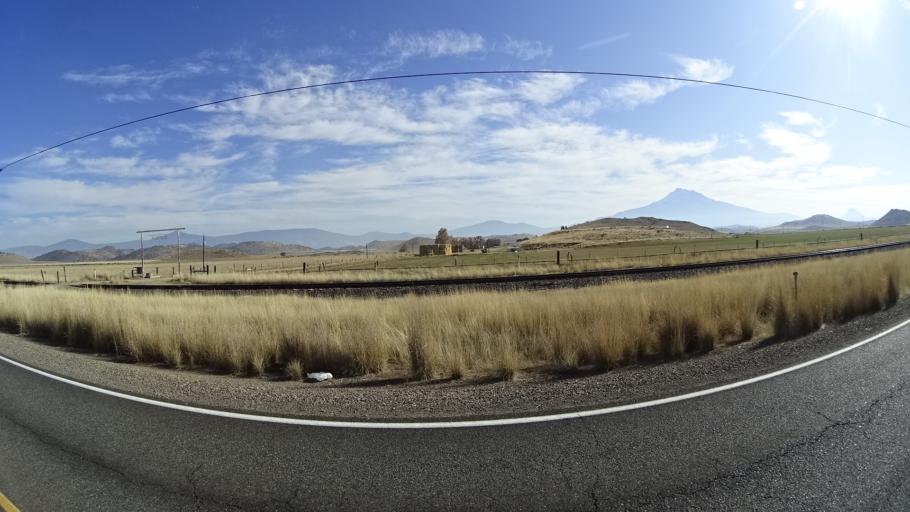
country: US
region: California
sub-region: Siskiyou County
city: Montague
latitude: 41.5645
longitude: -122.5256
